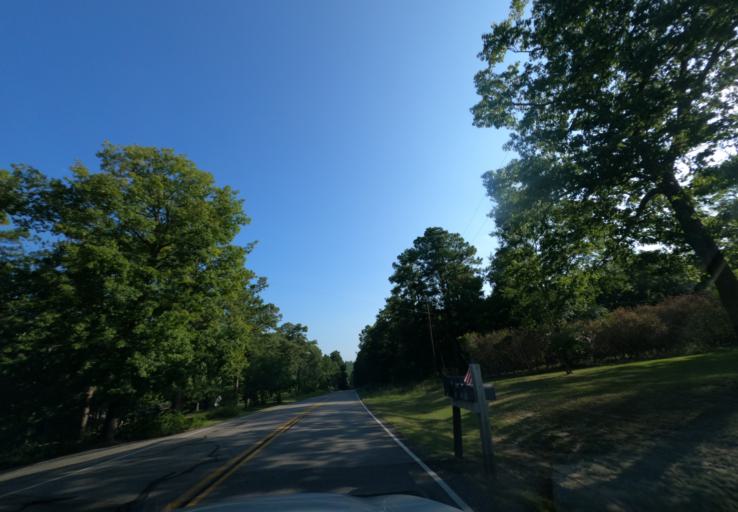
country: US
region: South Carolina
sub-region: Edgefield County
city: Murphys Estates
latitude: 33.5893
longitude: -81.9793
